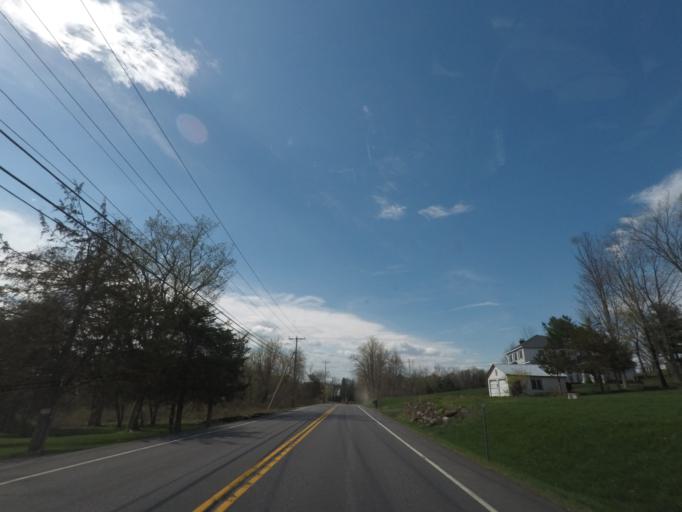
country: US
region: New York
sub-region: Greene County
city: Cairo
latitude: 42.3423
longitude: -74.0299
